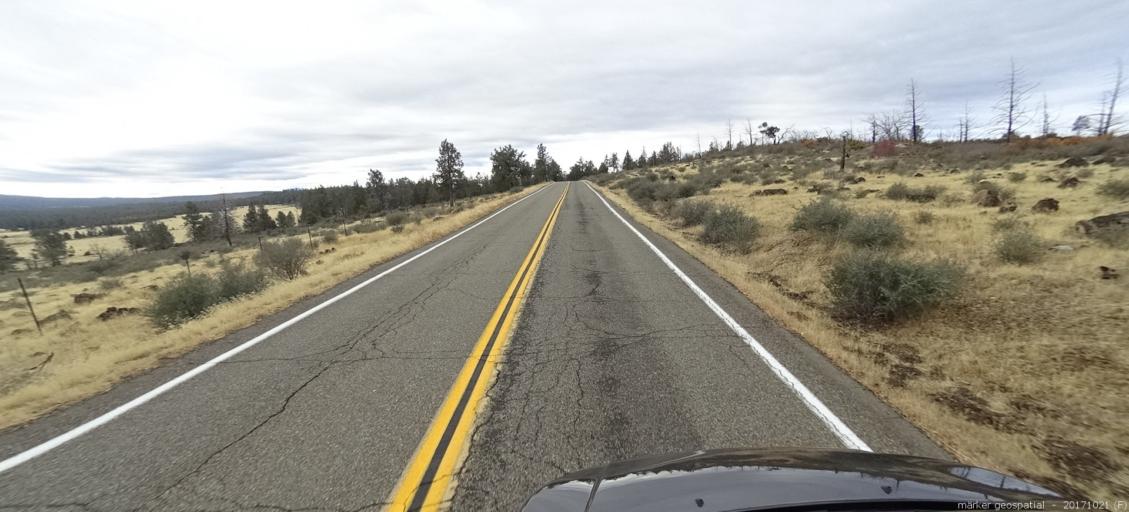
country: US
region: California
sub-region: Shasta County
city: Burney
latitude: 40.9345
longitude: -121.4523
